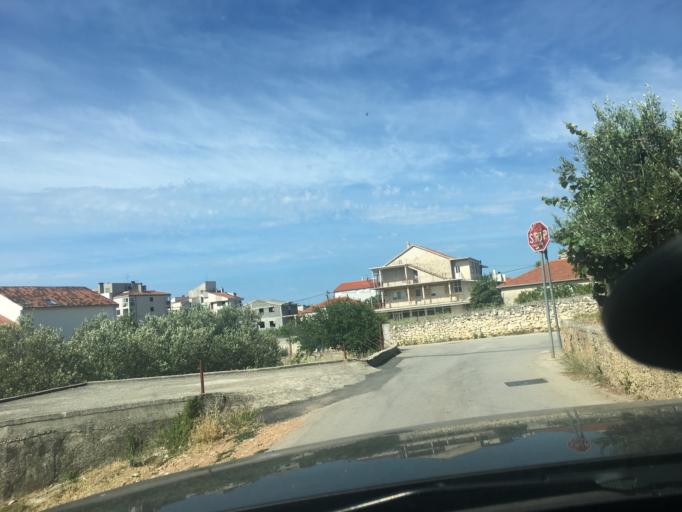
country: HR
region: Splitsko-Dalmatinska
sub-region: Grad Trogir
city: Trogir
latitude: 43.5224
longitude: 16.2576
